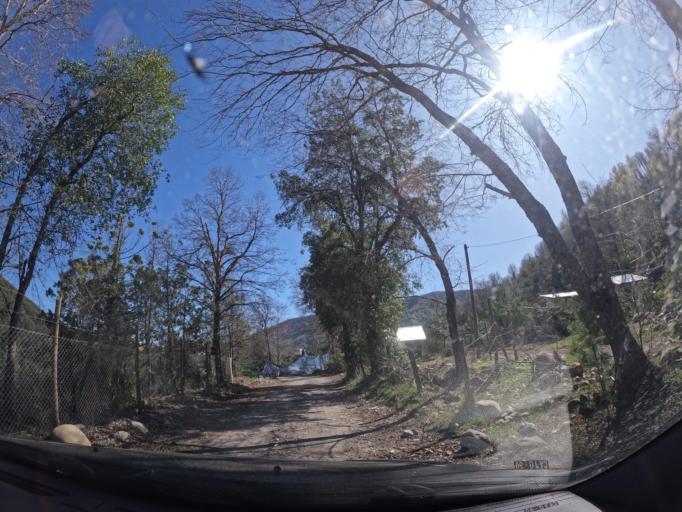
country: CL
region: Maule
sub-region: Provincia de Linares
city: Longavi
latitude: -36.2317
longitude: -71.3685
